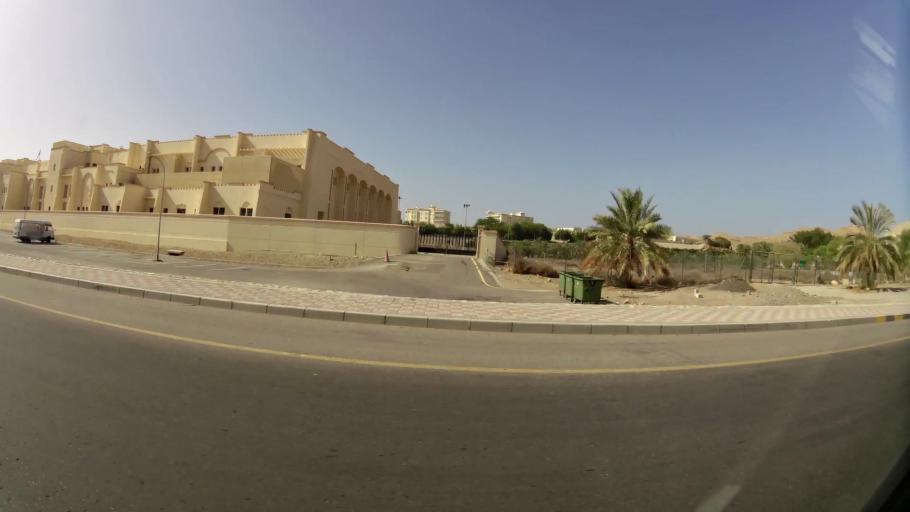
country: OM
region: Muhafazat Masqat
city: Muscat
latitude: 23.6162
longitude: 58.5125
